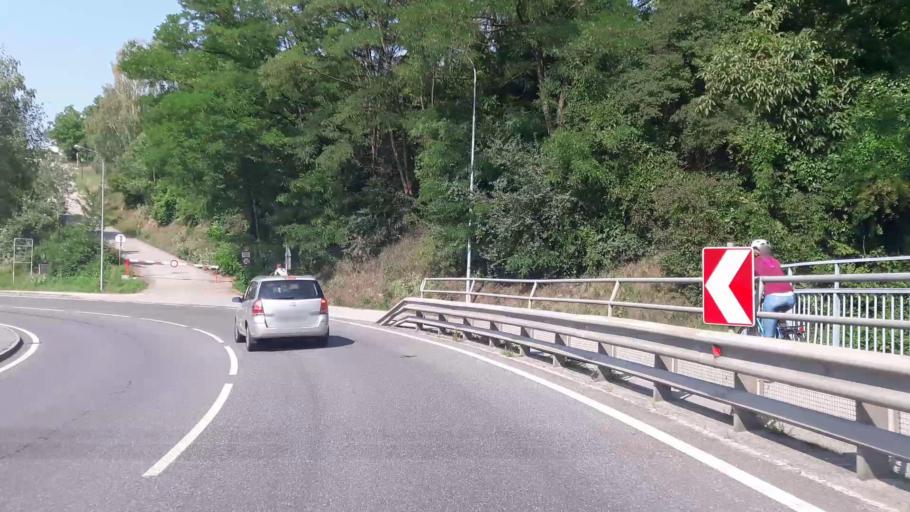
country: AT
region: Lower Austria
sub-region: Politischer Bezirk Melk
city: Emmersdorf an der Donau
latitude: 48.2458
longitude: 15.3416
